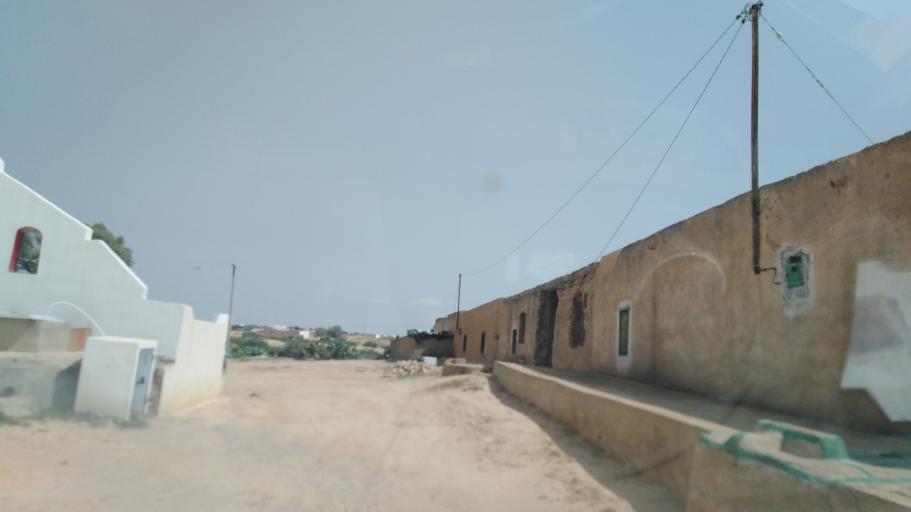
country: TN
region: Safaqis
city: Sfax
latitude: 34.6275
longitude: 10.5735
